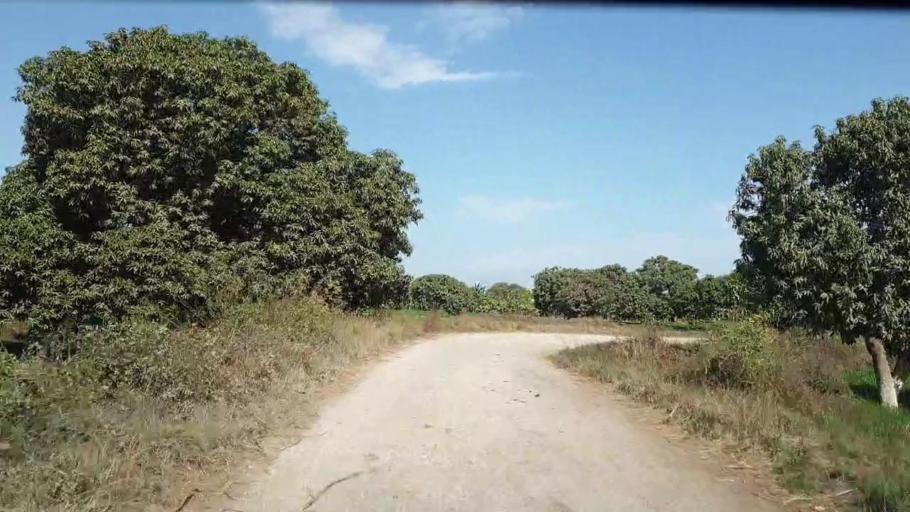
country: PK
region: Sindh
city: Matiari
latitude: 25.5282
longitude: 68.4958
